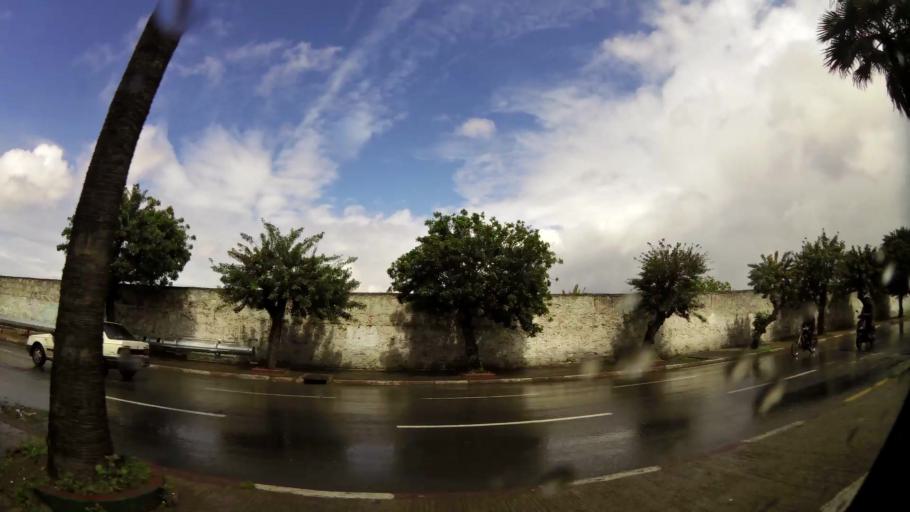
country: MA
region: Grand Casablanca
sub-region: Casablanca
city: Casablanca
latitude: 33.5466
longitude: -7.5642
